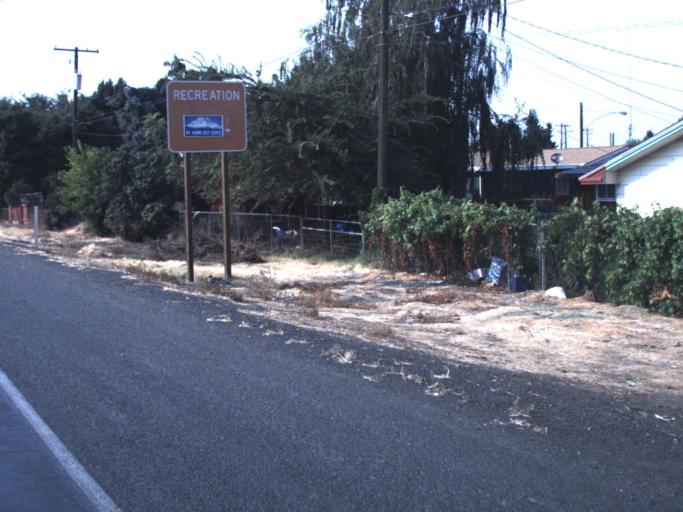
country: US
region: Washington
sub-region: Yakima County
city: Toppenish
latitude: 46.3688
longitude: -120.3171
